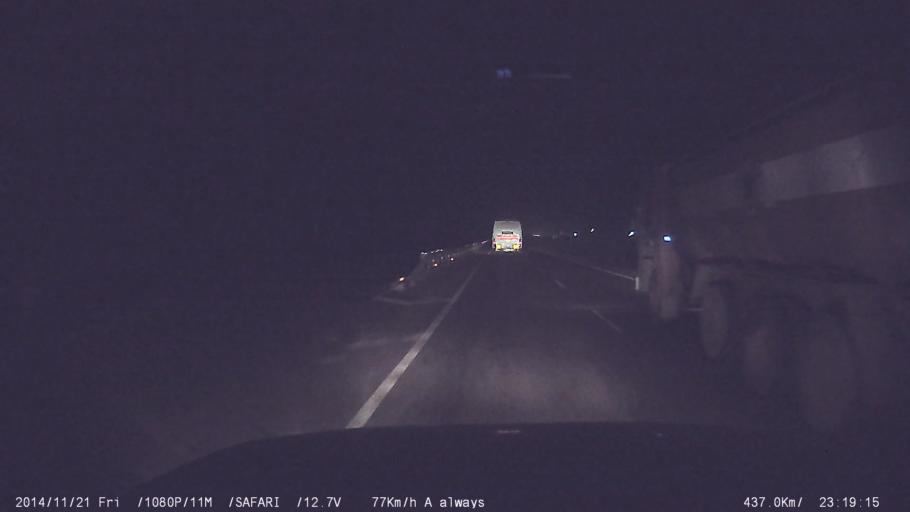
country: IN
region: Tamil Nadu
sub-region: Villupuram
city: Villupuram
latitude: 11.8863
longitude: 79.4549
